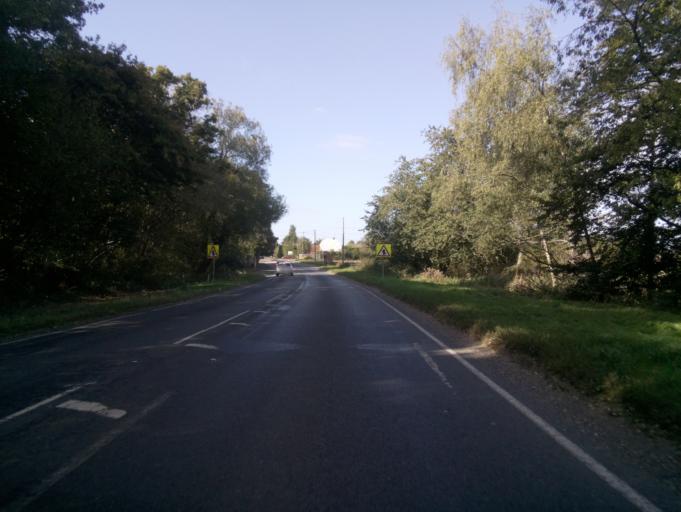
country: GB
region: England
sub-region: Hampshire
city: Tadley
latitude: 51.3198
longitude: -1.1217
